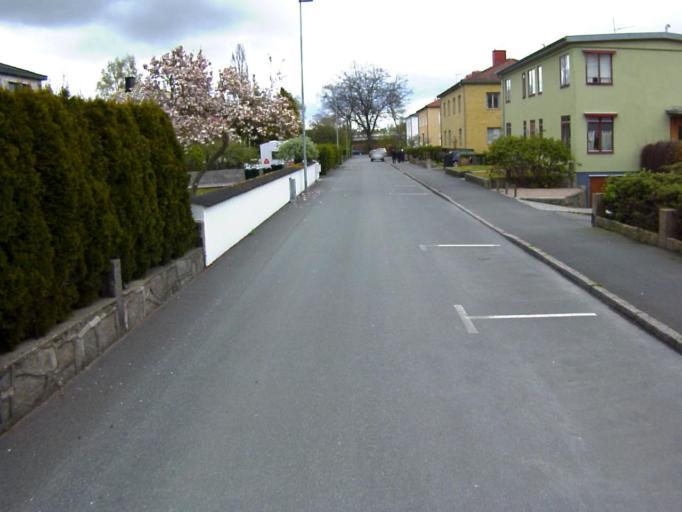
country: SE
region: Skane
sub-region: Kristianstads Kommun
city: Kristianstad
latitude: 56.0258
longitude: 14.1649
